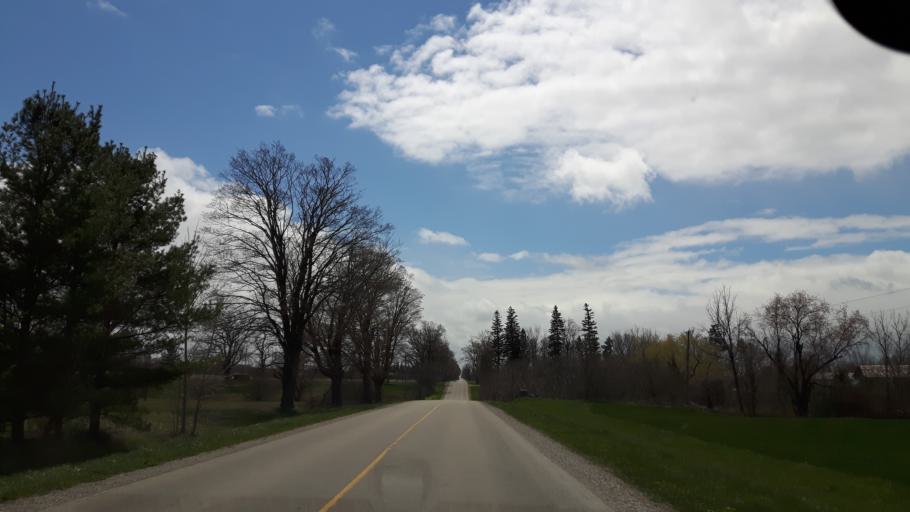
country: CA
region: Ontario
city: Bluewater
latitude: 43.5356
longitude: -81.6737
